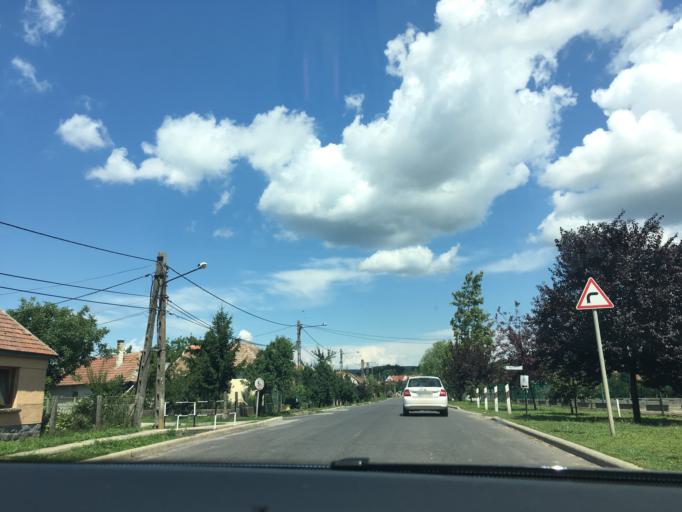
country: HU
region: Borsod-Abauj-Zemplen
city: Tarcal
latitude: 48.1553
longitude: 21.3621
